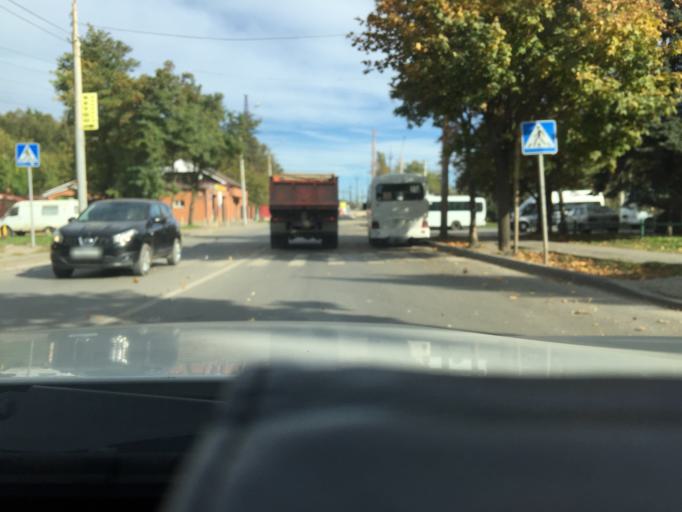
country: RU
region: Rostov
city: Imeni Chkalova
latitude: 47.2883
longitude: 39.8032
